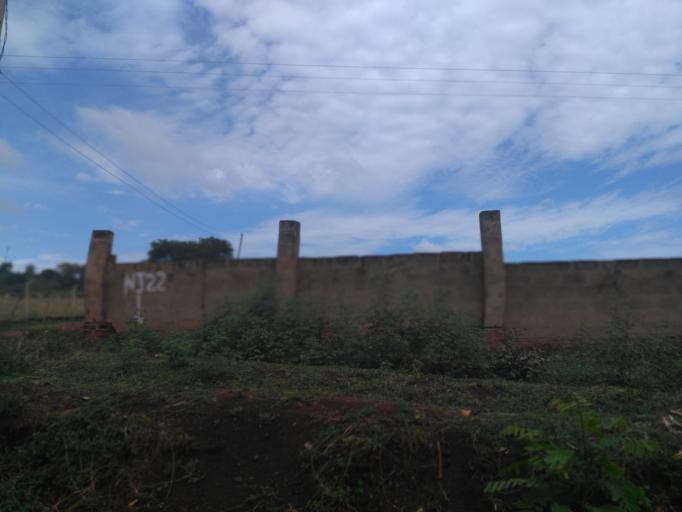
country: UG
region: Central Region
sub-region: Buikwe District
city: Njeru
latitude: 0.4177
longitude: 33.1846
